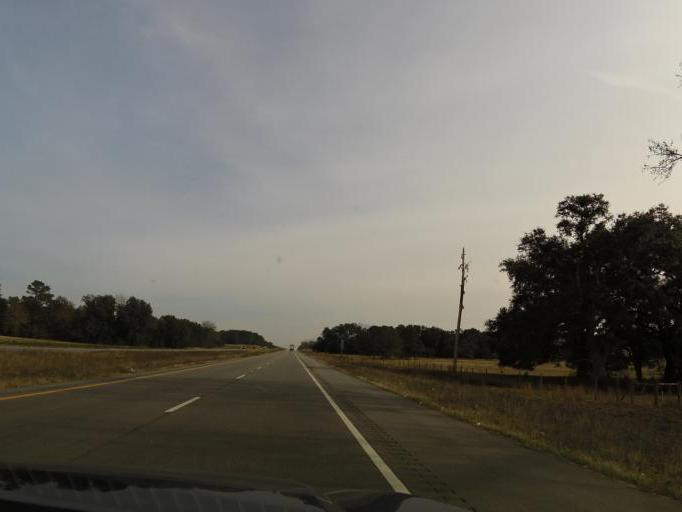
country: US
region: Alabama
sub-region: Houston County
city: Ashford
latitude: 31.1711
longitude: -85.2226
